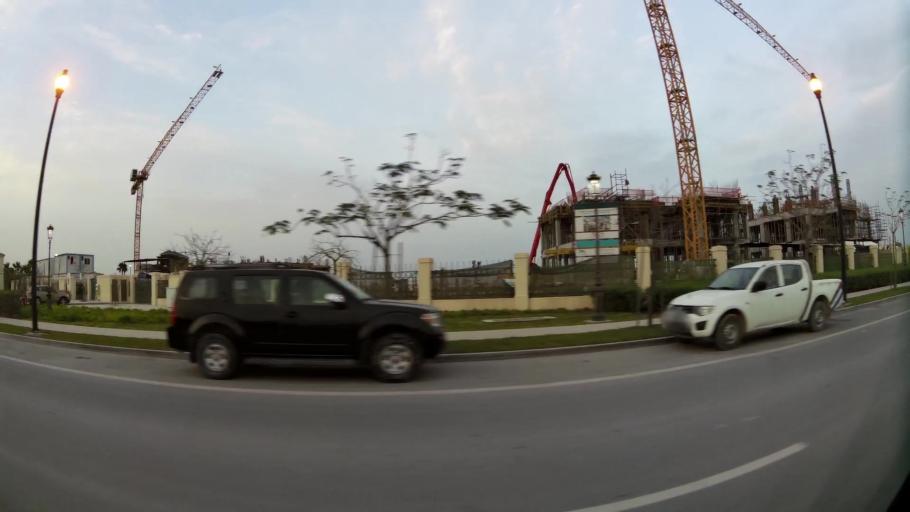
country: QA
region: Baladiyat ad Dawhah
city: Doha
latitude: 25.3606
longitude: 51.5666
